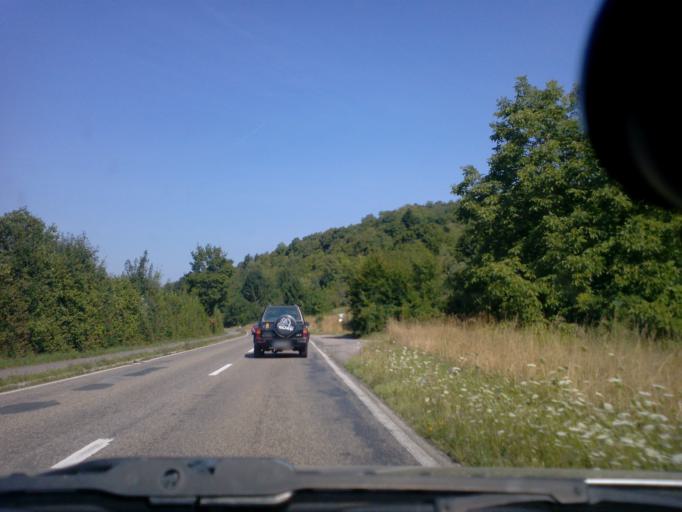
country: DE
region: Baden-Wuerttemberg
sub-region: Karlsruhe Region
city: Joehlingen
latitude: 49.0804
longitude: 8.5688
